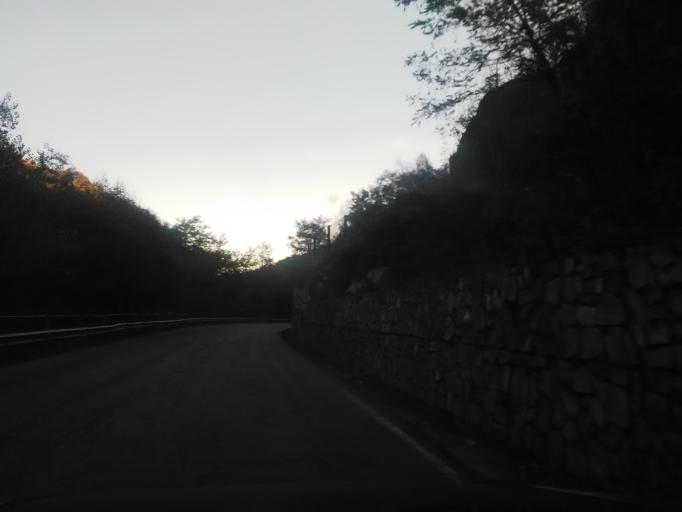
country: IT
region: Piedmont
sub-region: Provincia di Biella
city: Crevacuore
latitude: 45.6874
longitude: 8.2584
